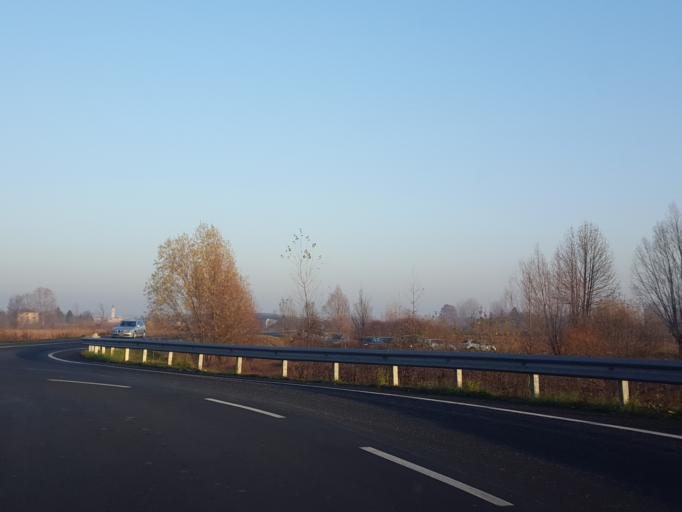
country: IT
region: Veneto
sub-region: Provincia di Vicenza
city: Torri di Quartesolo
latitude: 45.5140
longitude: 11.6381
